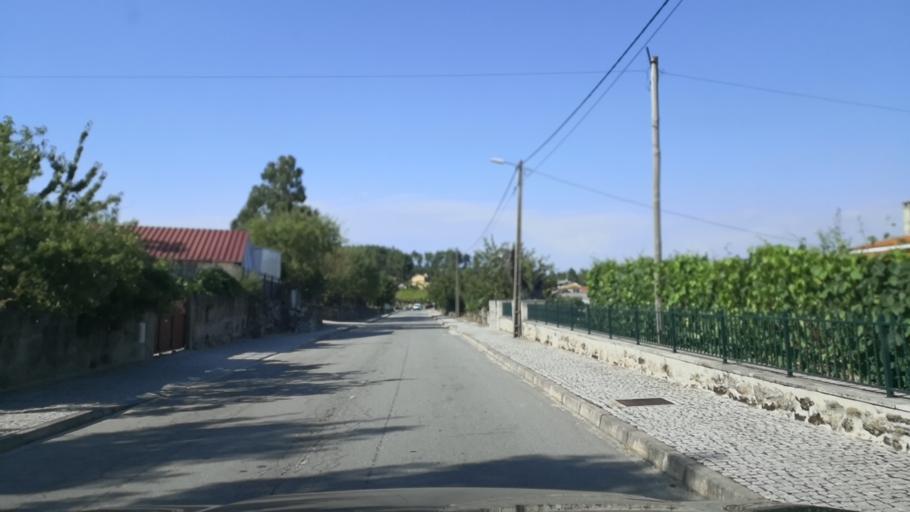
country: PT
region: Vila Real
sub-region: Murca
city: Murca
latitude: 41.3758
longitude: -7.5032
